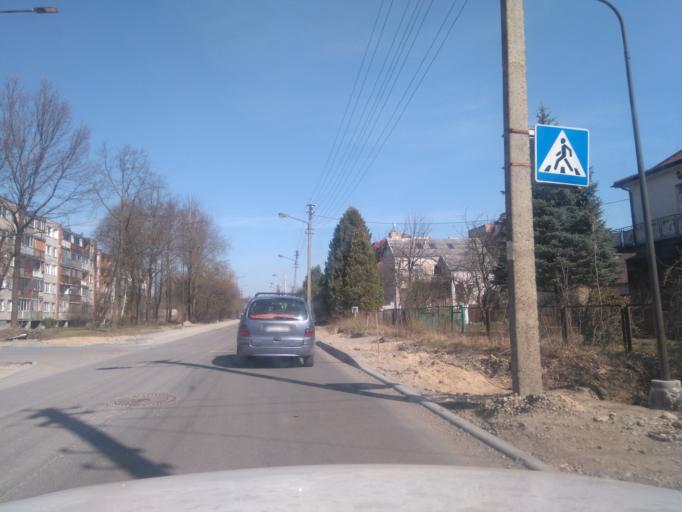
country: LT
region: Kauno apskritis
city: Dainava (Kaunas)
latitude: 54.8906
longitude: 23.9545
